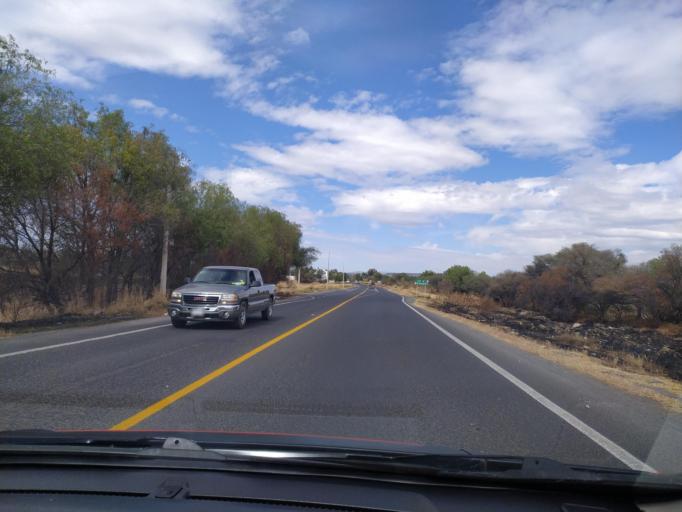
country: LA
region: Oudomxai
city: Muang La
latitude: 21.0098
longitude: 101.8291
